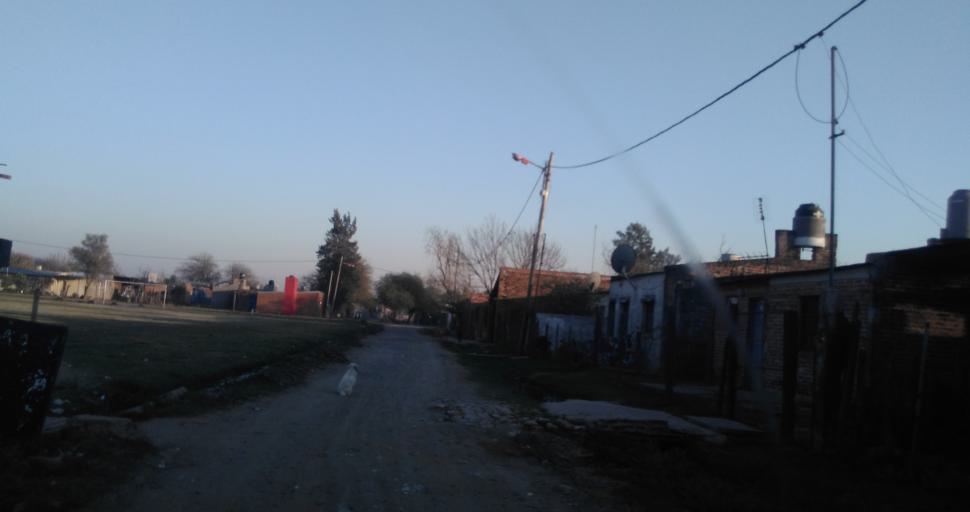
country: AR
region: Chaco
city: Resistencia
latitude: -27.4653
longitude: -59.0196
